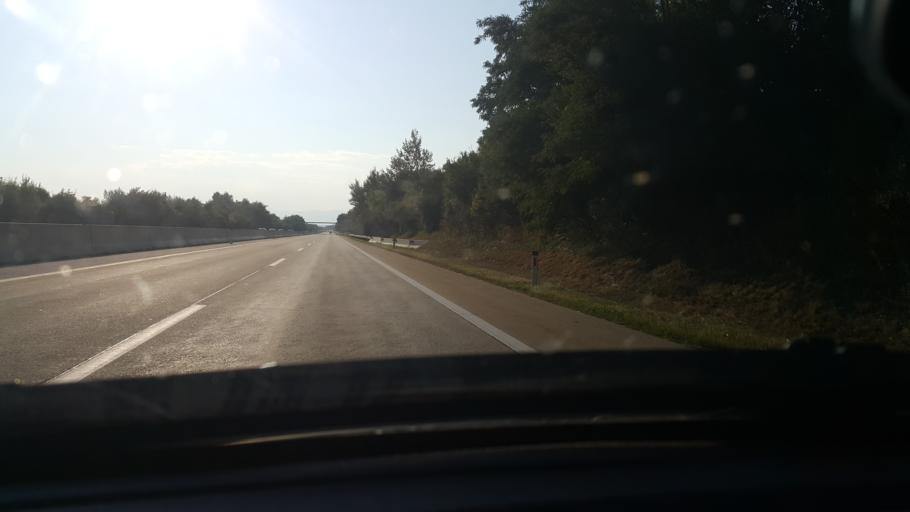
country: AT
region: Carinthia
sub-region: Politischer Bezirk Klagenfurt Land
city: Ebenthal
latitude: 46.6416
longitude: 14.3577
